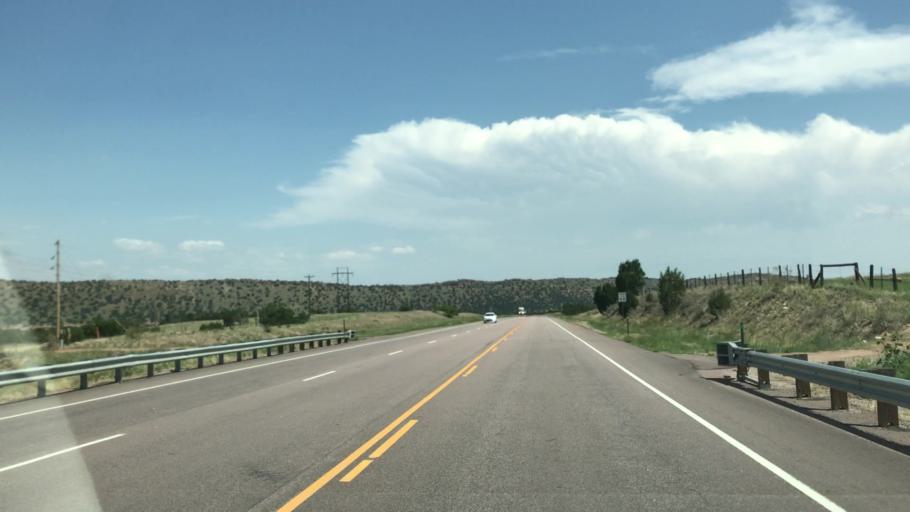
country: US
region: Colorado
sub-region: Fremont County
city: Canon City
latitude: 38.4875
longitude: -105.2760
